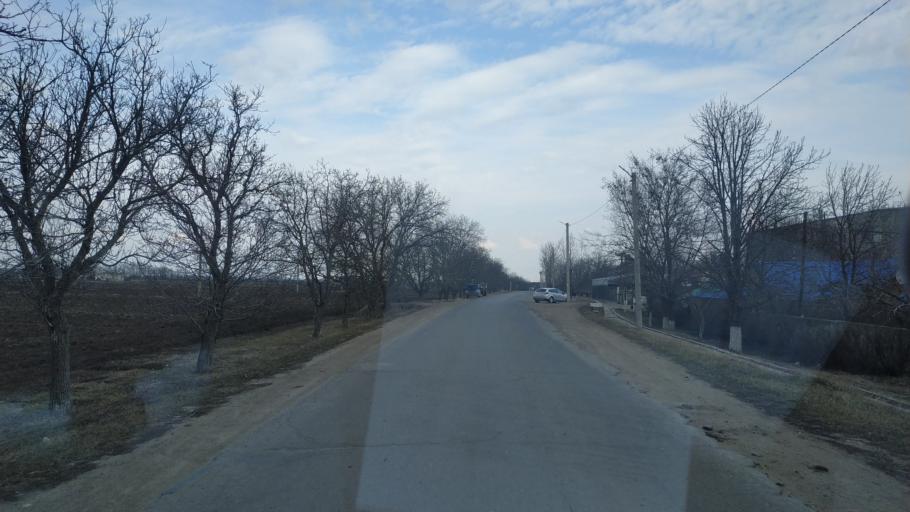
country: MD
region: Anenii Noi
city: Anenii Noi
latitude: 46.8987
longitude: 29.3091
